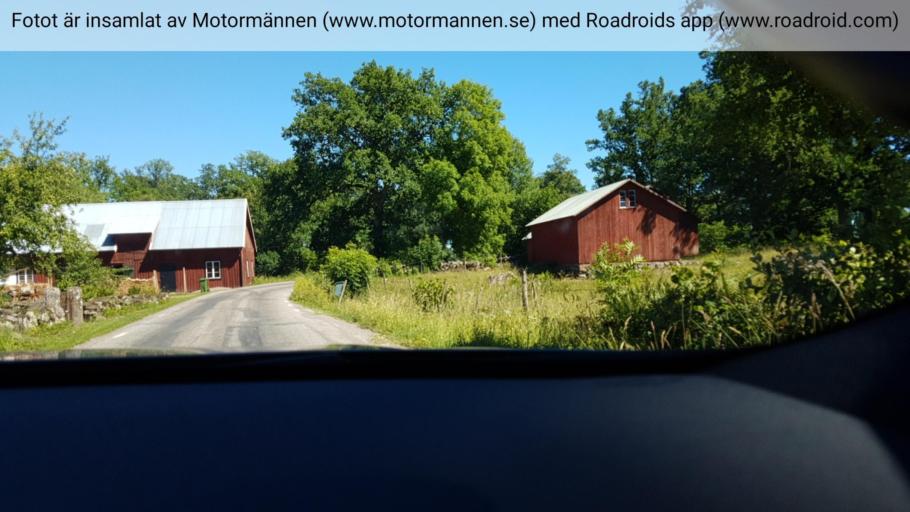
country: SE
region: Vaestra Goetaland
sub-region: Falkopings Kommun
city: Floby
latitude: 58.0663
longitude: 13.4350
